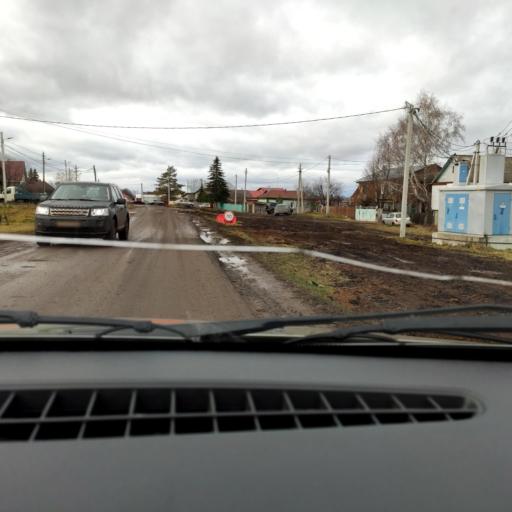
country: RU
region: Bashkortostan
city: Avdon
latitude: 54.4982
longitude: 55.8775
